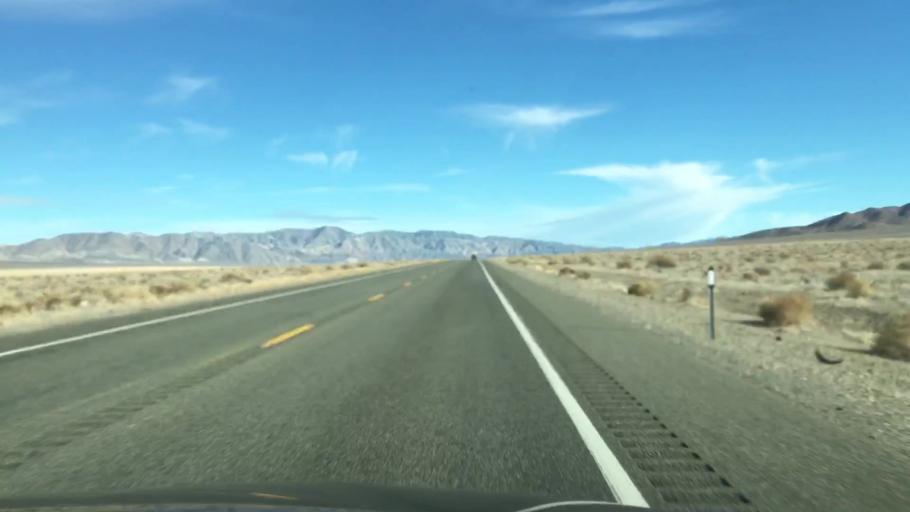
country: US
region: Nevada
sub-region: Mineral County
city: Hawthorne
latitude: 38.5370
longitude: -118.3335
